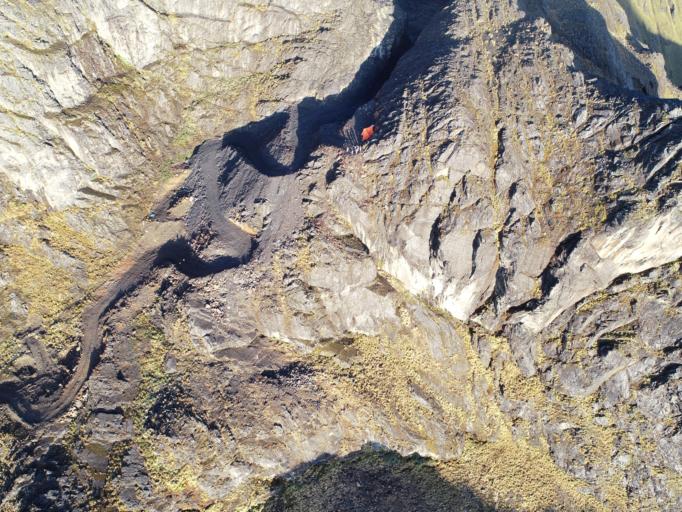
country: PE
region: Puno
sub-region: San Antonio De Putina
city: Sina
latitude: -14.7371
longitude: -69.0489
